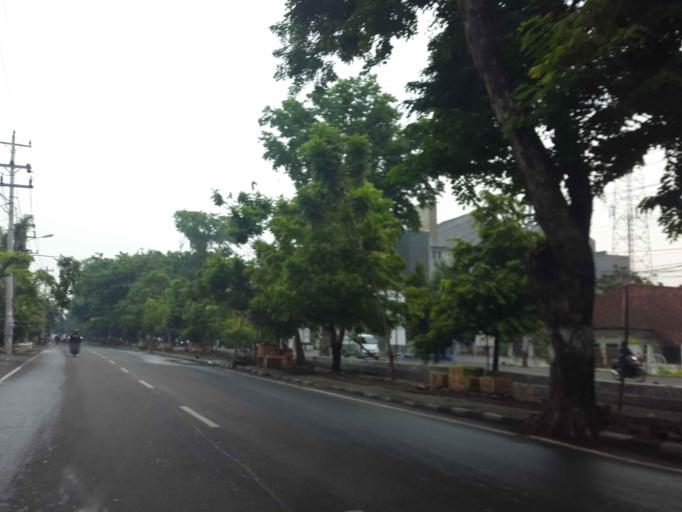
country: ID
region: Central Java
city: Semarang
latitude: -6.9858
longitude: 110.4224
